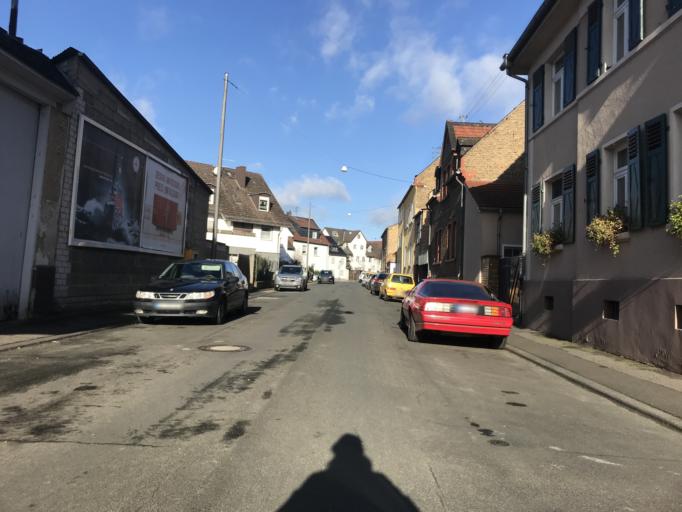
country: DE
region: Hesse
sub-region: Regierungsbezirk Darmstadt
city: Hochheim am Main
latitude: 50.0540
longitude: 8.3065
